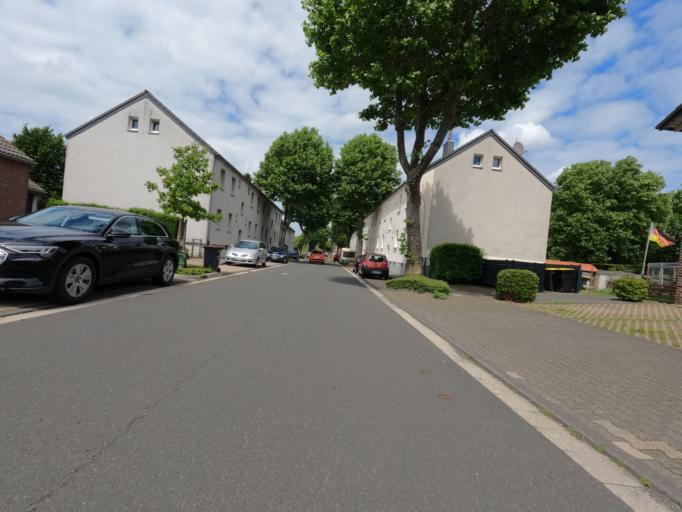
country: DE
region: North Rhine-Westphalia
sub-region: Regierungsbezirk Koln
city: Ubach-Palenberg
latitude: 50.9104
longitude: 6.1412
